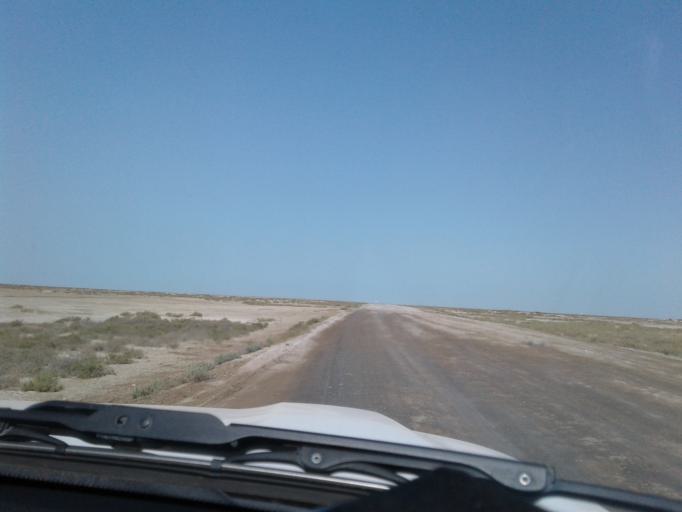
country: IR
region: Golestan
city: Gomishan
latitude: 37.8399
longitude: 53.8936
